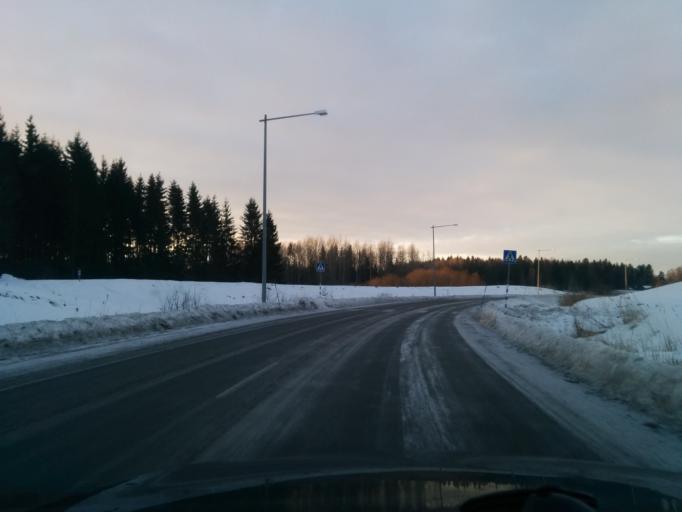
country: SE
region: Uppsala
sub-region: Tierps Kommun
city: Orbyhus
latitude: 60.2242
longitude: 17.7082
